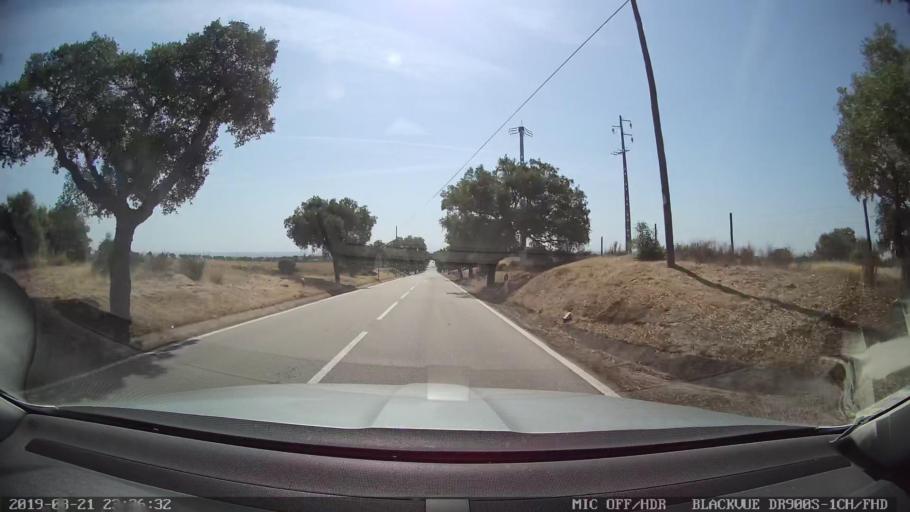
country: PT
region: Guarda
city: Alcains
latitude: 39.8751
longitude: -7.3735
